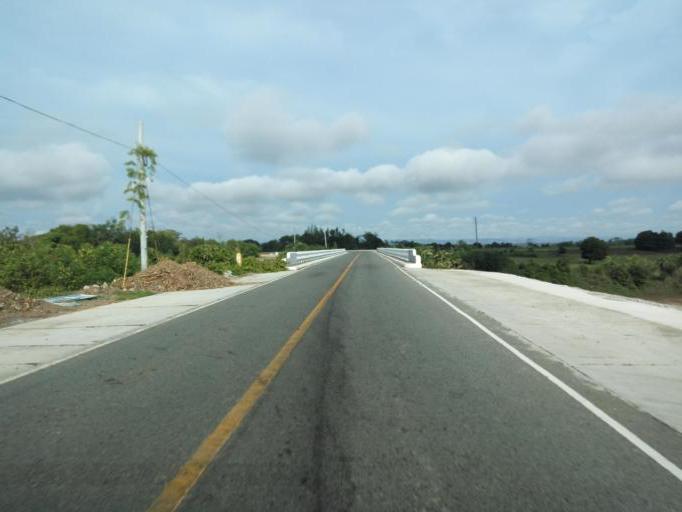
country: PH
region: Cagayan Valley
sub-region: Province of Isabela
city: Masipi West
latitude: 17.3678
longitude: 121.8214
